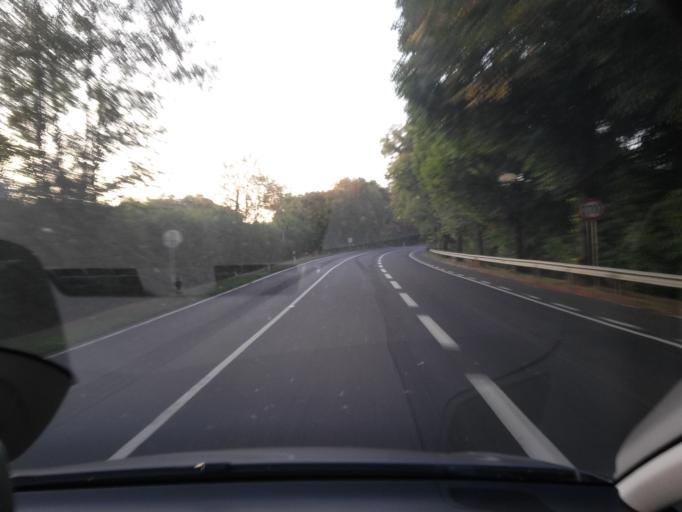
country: LU
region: Luxembourg
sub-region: Canton de Luxembourg
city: Alzingen
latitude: 49.5436
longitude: 6.1744
